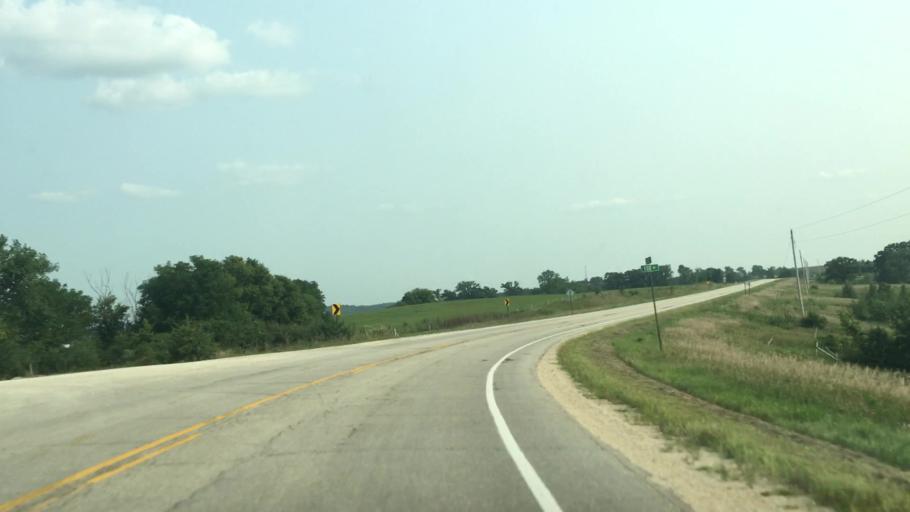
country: US
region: Minnesota
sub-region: Fillmore County
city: Preston
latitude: 43.6887
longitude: -91.9436
